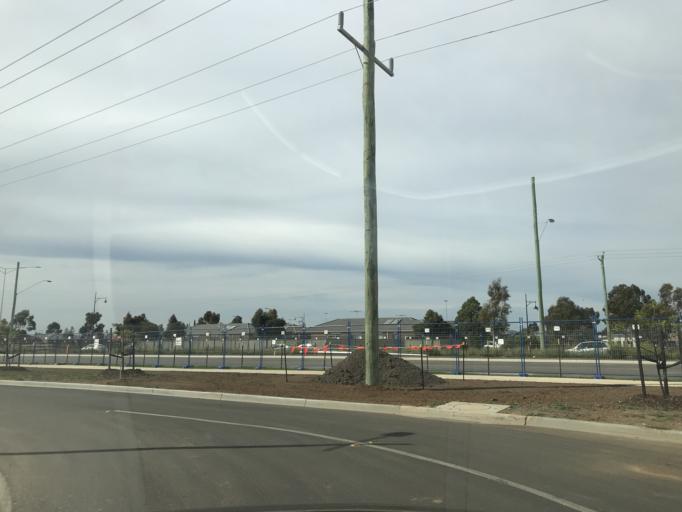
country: AU
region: Victoria
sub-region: Wyndham
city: Williams Landing
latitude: -37.8362
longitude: 144.7154
